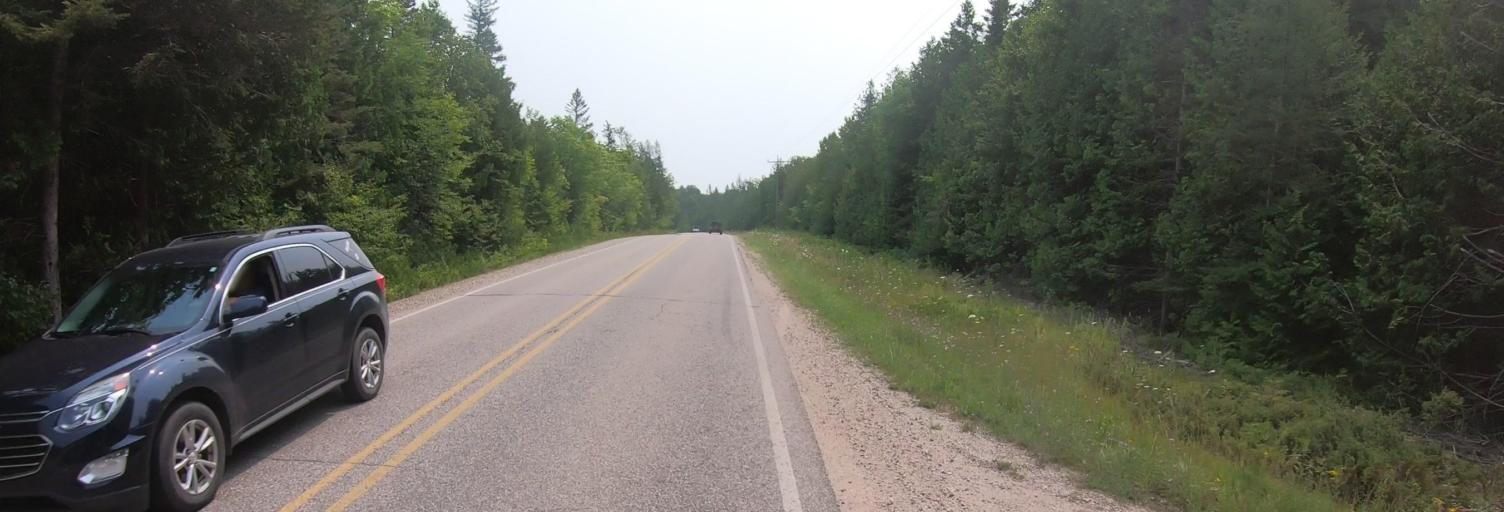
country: CA
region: Ontario
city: Thessalon
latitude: 45.9956
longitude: -83.7071
